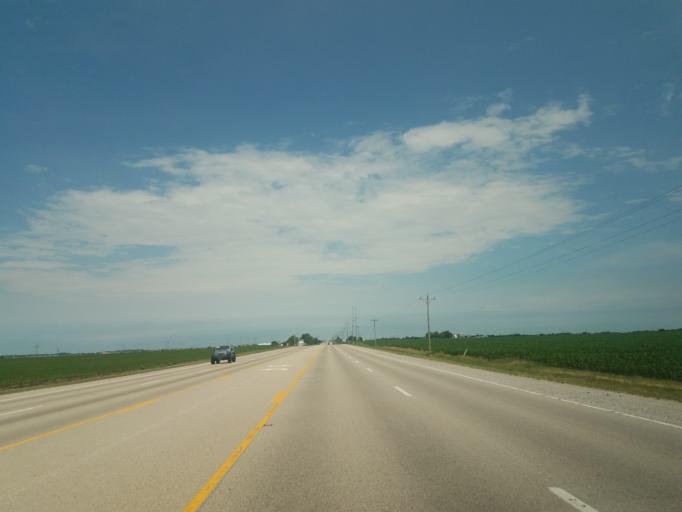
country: US
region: Illinois
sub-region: McLean County
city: Downs
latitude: 40.4300
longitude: -88.9015
